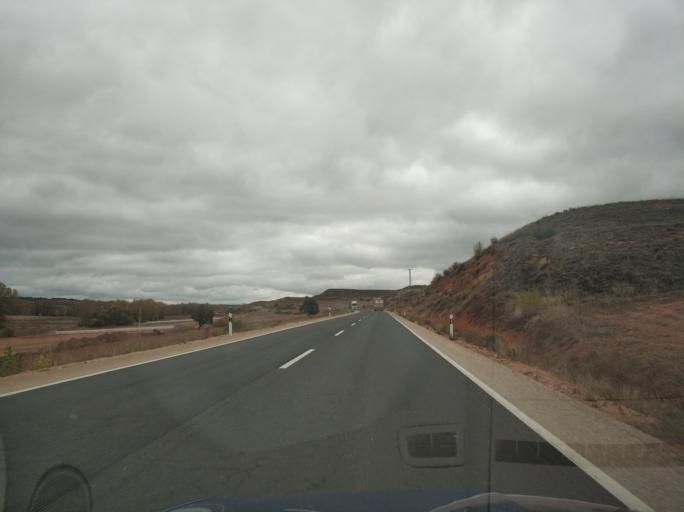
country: ES
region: Castille and Leon
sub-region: Provincia de Soria
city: San Esteban de Gormaz
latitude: 41.5796
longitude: -3.2212
